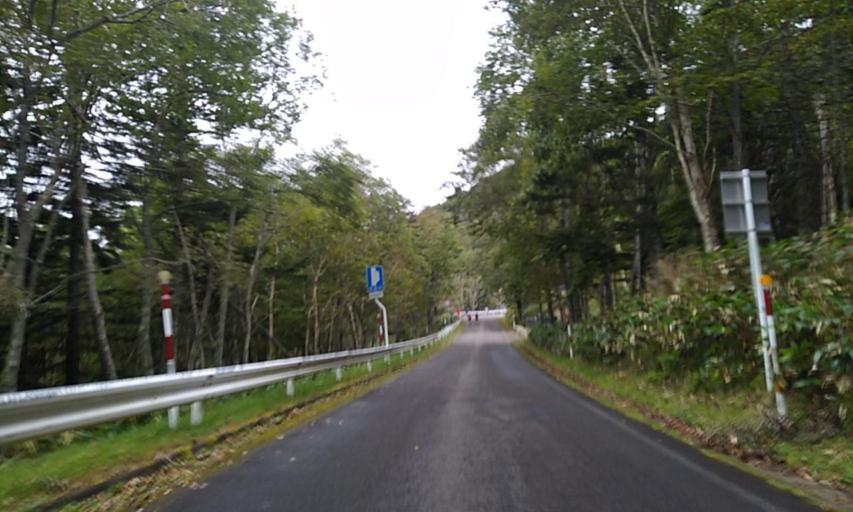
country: JP
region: Hokkaido
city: Bihoro
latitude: 43.5808
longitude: 144.2339
